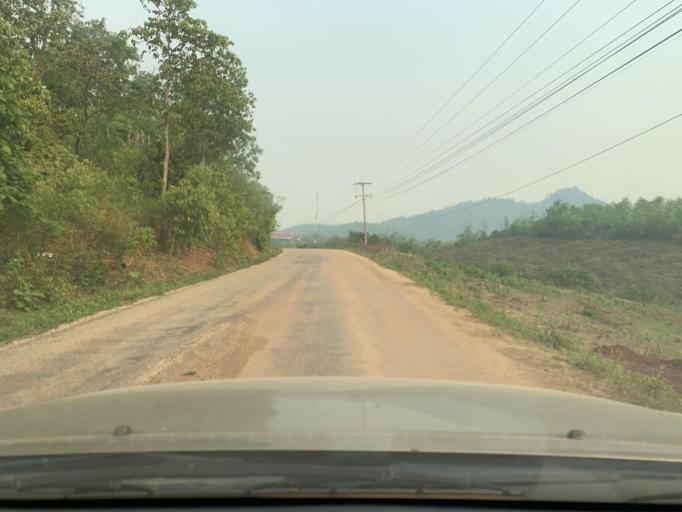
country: LA
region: Louangphabang
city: Louangphabang
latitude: 19.9115
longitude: 102.0795
